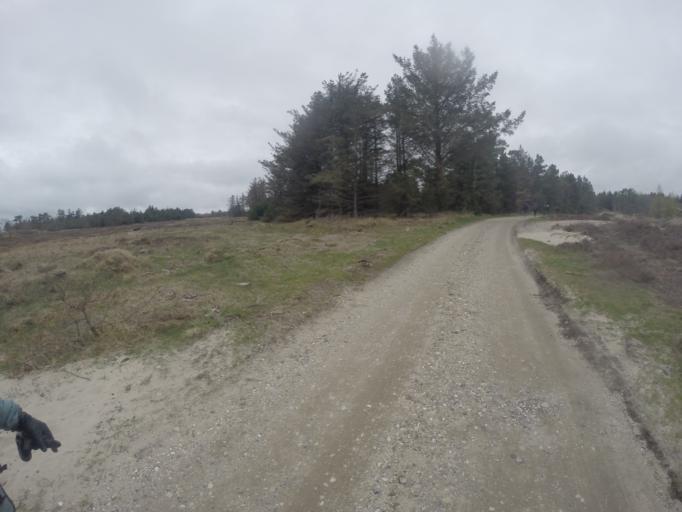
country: DK
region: North Denmark
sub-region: Thisted Kommune
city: Hurup
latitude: 56.8730
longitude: 8.3092
